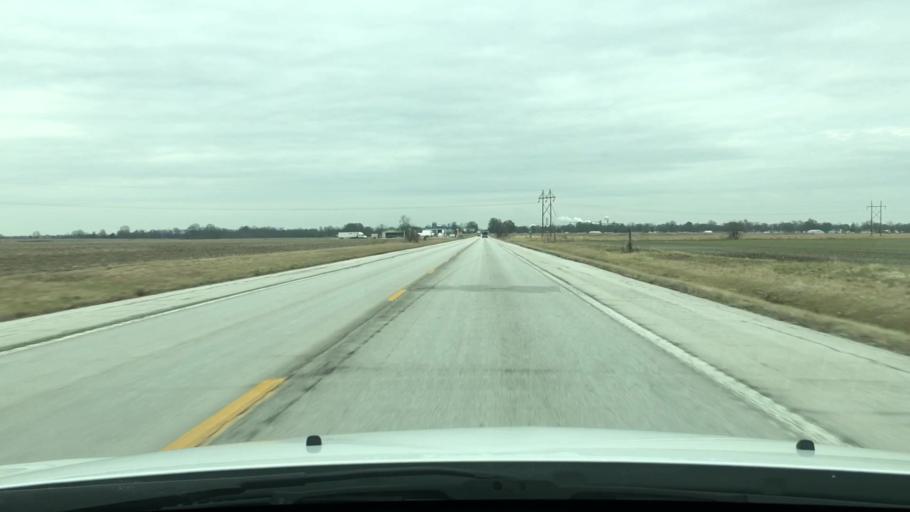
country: US
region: Missouri
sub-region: Montgomery County
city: Wellsville
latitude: 39.2236
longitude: -91.6462
